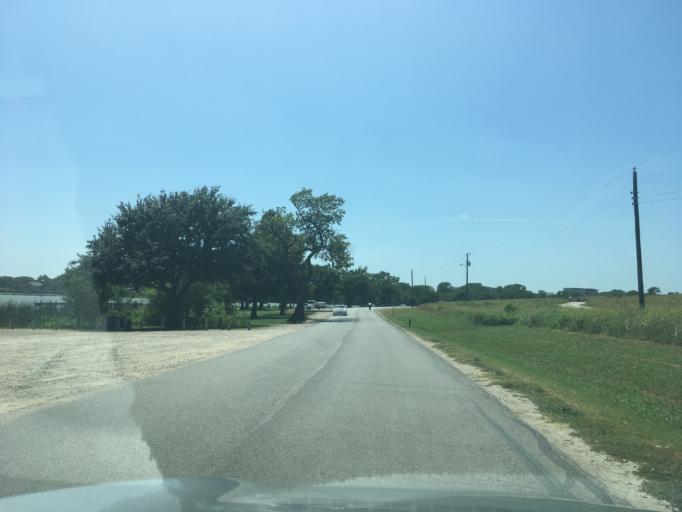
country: US
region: Texas
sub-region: Dallas County
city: Highland Park
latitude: 32.8505
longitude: -96.7193
